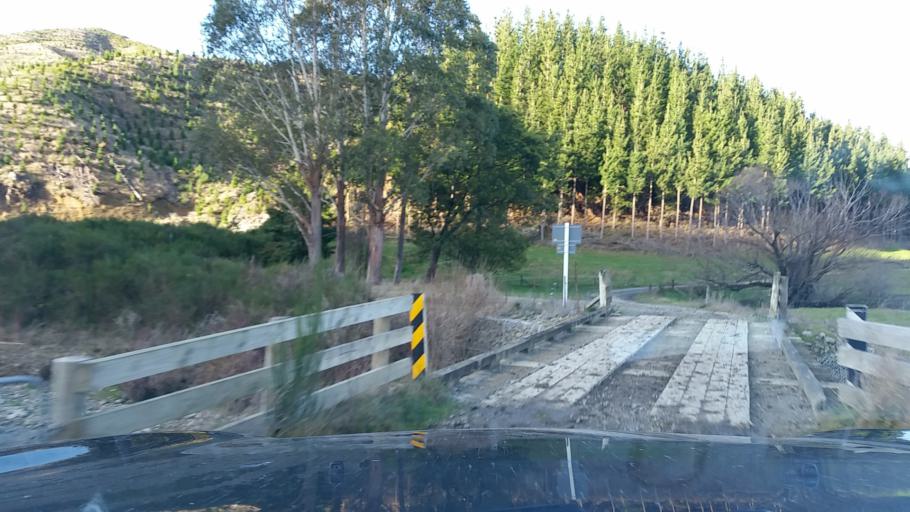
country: NZ
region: Nelson
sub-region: Nelson City
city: Nelson
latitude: -41.5332
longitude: 173.4889
